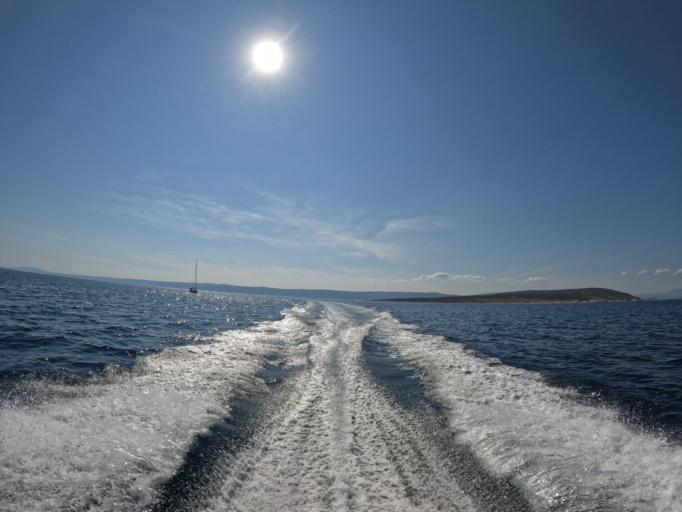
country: HR
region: Primorsko-Goranska
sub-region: Grad Krk
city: Krk
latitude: 44.9541
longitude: 14.5668
